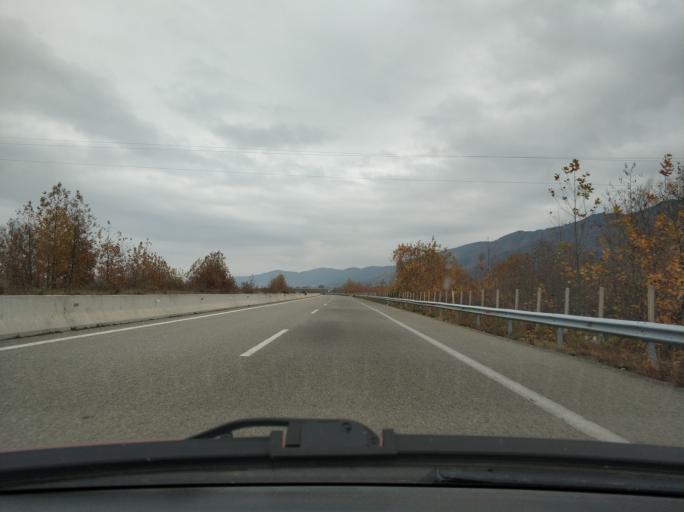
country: GR
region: East Macedonia and Thrace
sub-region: Nomos Kavalas
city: Eleftheres
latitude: 40.8644
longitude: 24.1840
